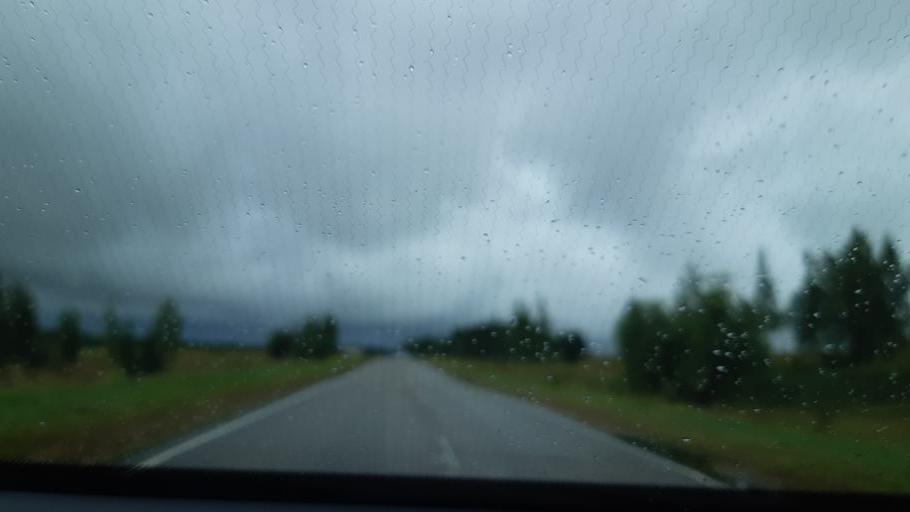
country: RU
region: Smolensk
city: Gagarin
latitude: 55.6324
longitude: 34.9606
